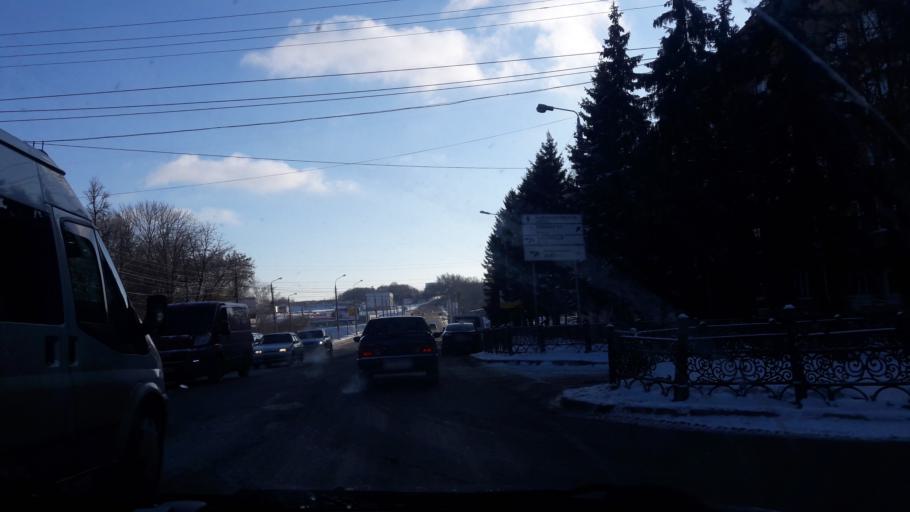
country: RU
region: Tula
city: Tula
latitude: 54.1740
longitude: 37.6338
